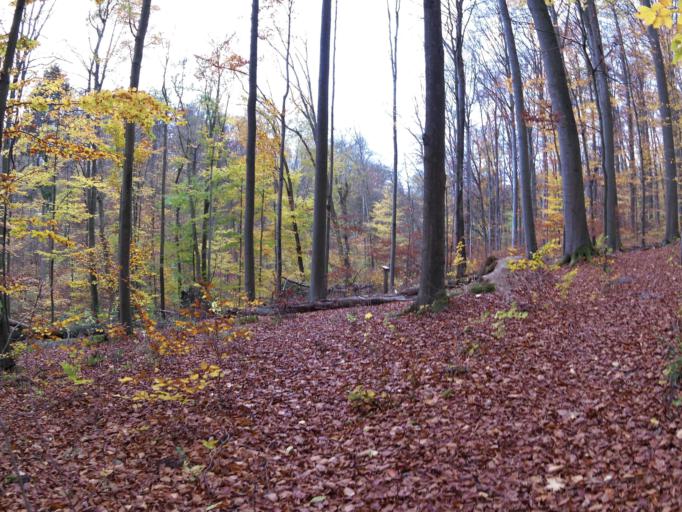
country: DE
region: Thuringia
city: Bischofroda
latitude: 51.0759
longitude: 10.3819
